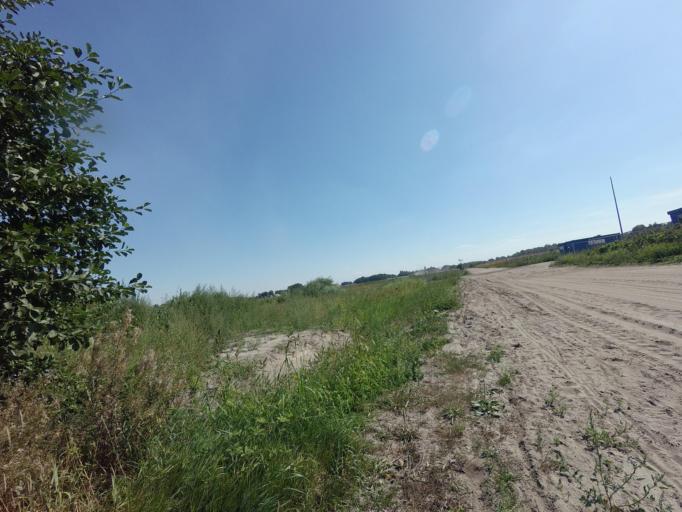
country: NL
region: North Brabant
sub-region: Gemeente Someren
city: Someren
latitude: 51.3846
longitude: 5.6682
